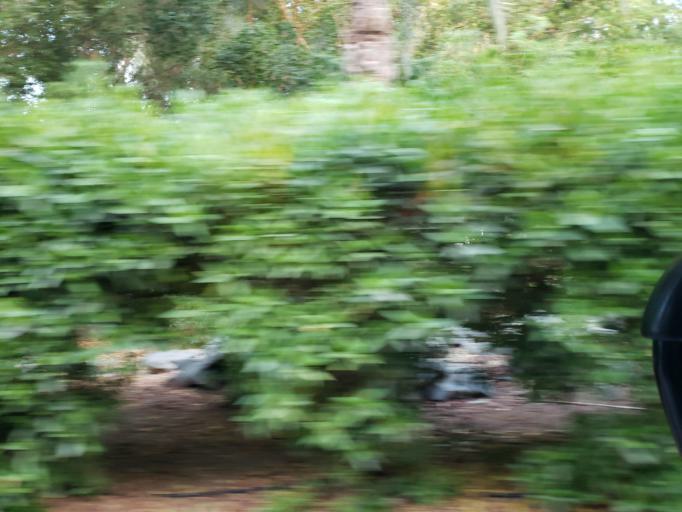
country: AE
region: Dubai
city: Dubai
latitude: 24.9853
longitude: 55.0226
